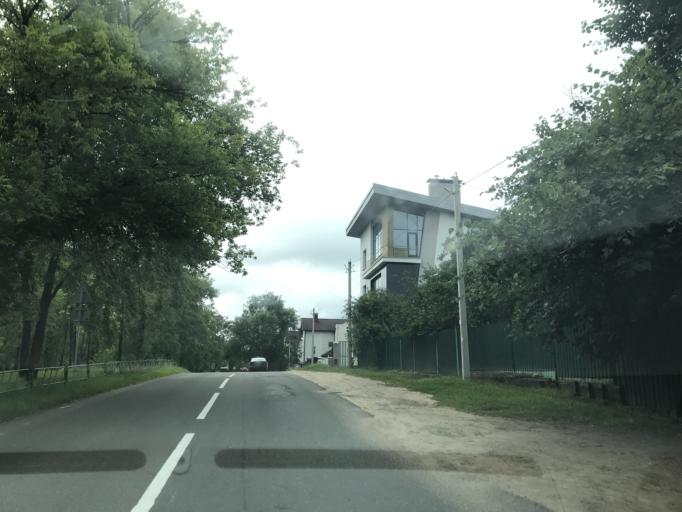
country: BY
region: Minsk
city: Minsk
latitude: 53.9387
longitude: 27.6213
